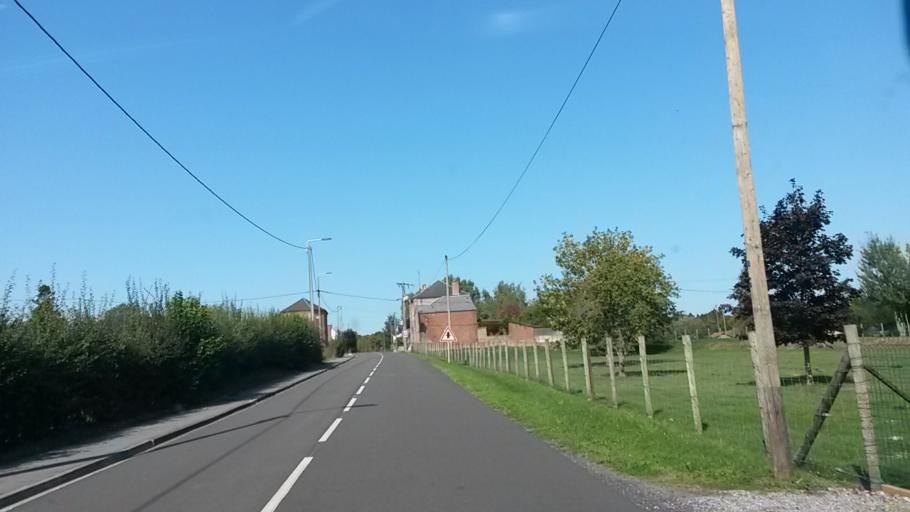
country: FR
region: Nord-Pas-de-Calais
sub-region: Departement du Nord
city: Avesnelles
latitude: 50.1221
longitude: 3.9438
